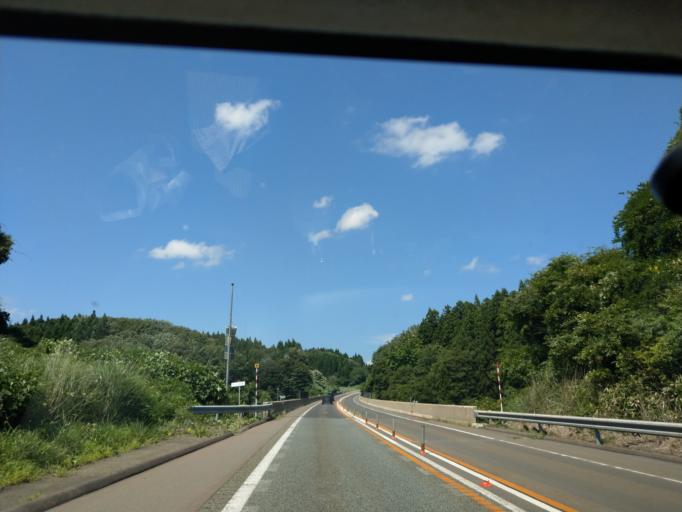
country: JP
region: Akita
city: Akita
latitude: 39.6761
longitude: 140.1862
